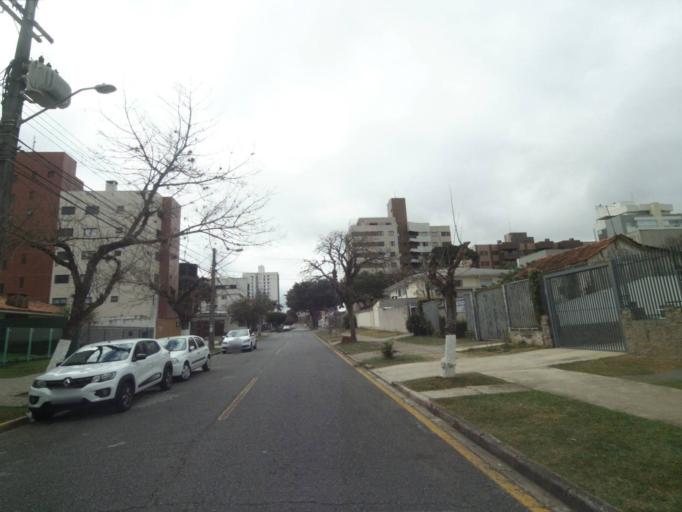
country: BR
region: Parana
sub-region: Curitiba
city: Curitiba
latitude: -25.4603
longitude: -49.2933
